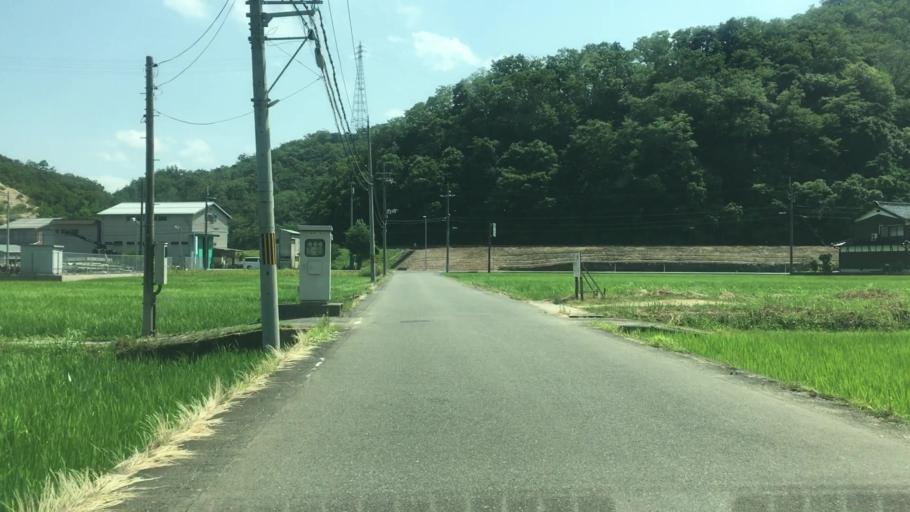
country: JP
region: Hyogo
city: Toyooka
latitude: 35.5664
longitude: 134.7918
